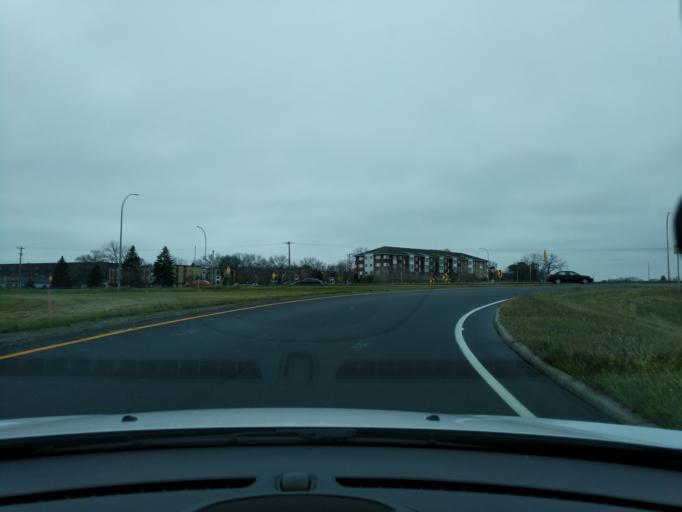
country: US
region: Minnesota
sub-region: Ramsey County
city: Roseville
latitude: 45.0093
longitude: -93.1655
